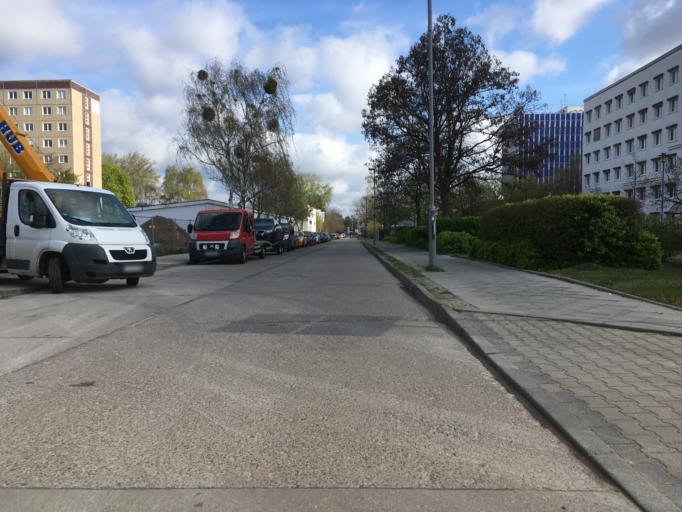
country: DE
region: Berlin
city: Friedrichsfelde
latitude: 52.5275
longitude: 13.5292
